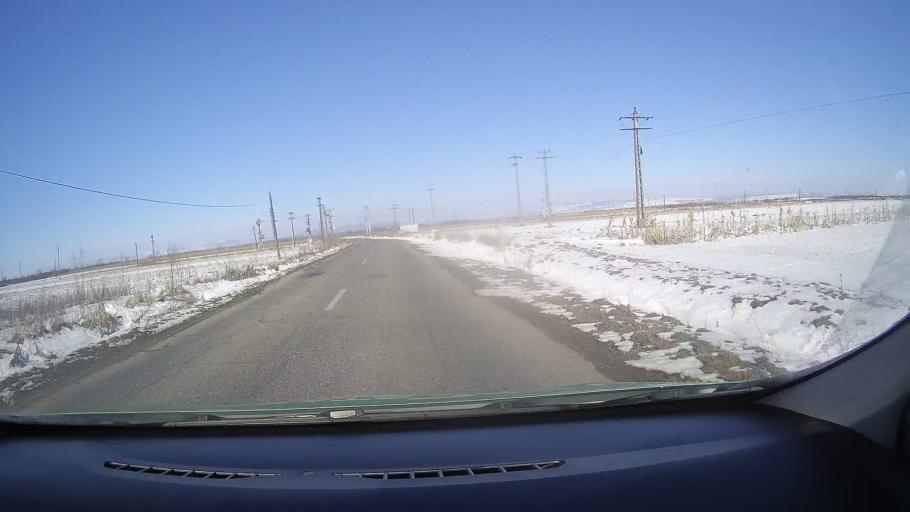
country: RO
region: Brasov
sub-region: Comuna Harseni
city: Harseni
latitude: 45.7622
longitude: 25.0072
